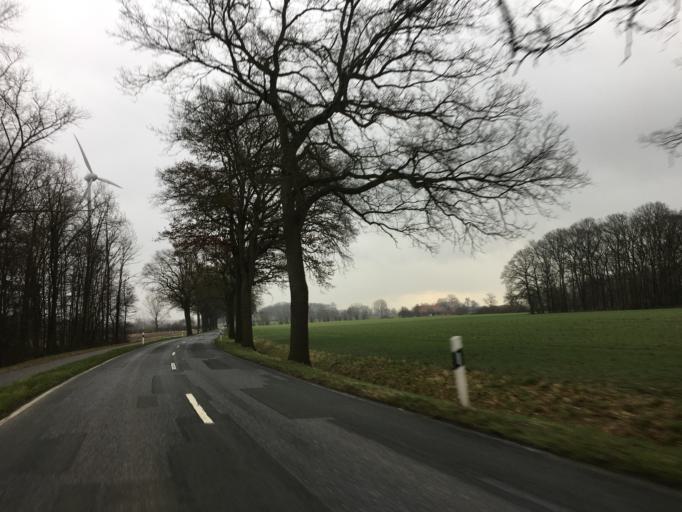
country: DE
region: North Rhine-Westphalia
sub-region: Regierungsbezirk Munster
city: Nottuln
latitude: 51.8631
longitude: 7.3950
